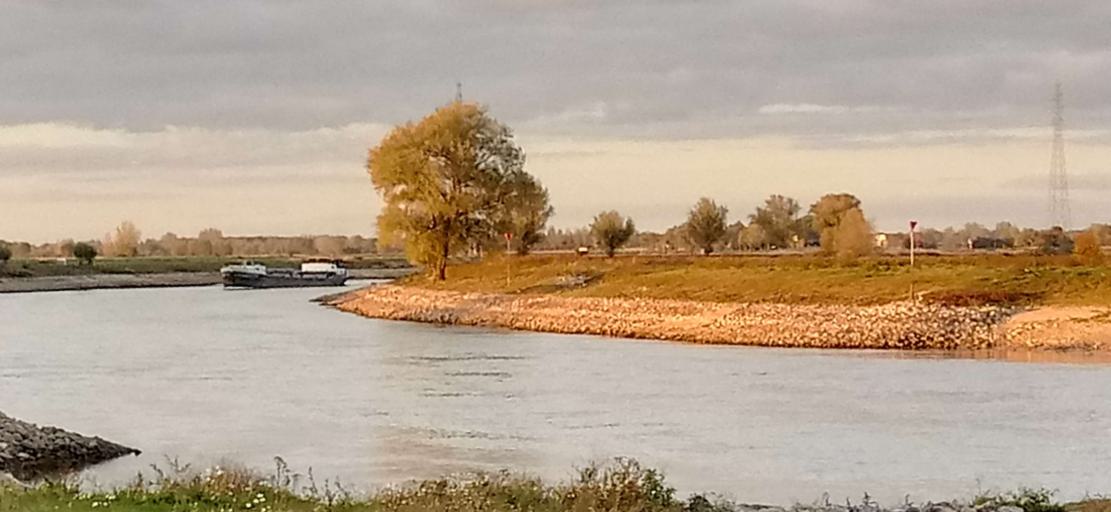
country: NL
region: Gelderland
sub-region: Gemeente Zutphen
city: Zutphen
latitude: 52.1492
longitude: 6.1816
